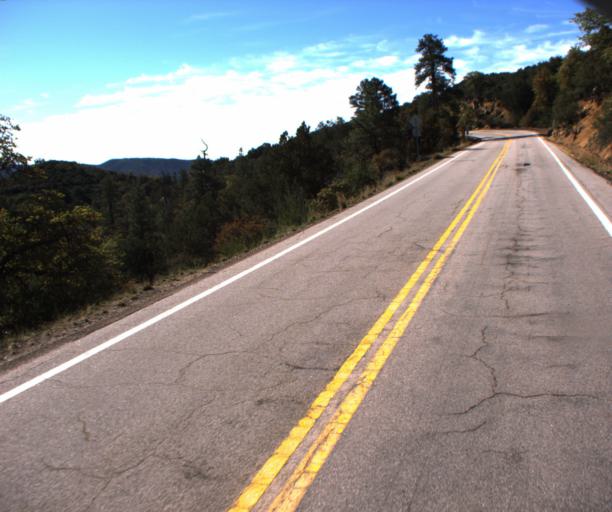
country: US
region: Arizona
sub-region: Yavapai County
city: Prescott
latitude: 34.4380
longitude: -112.5462
